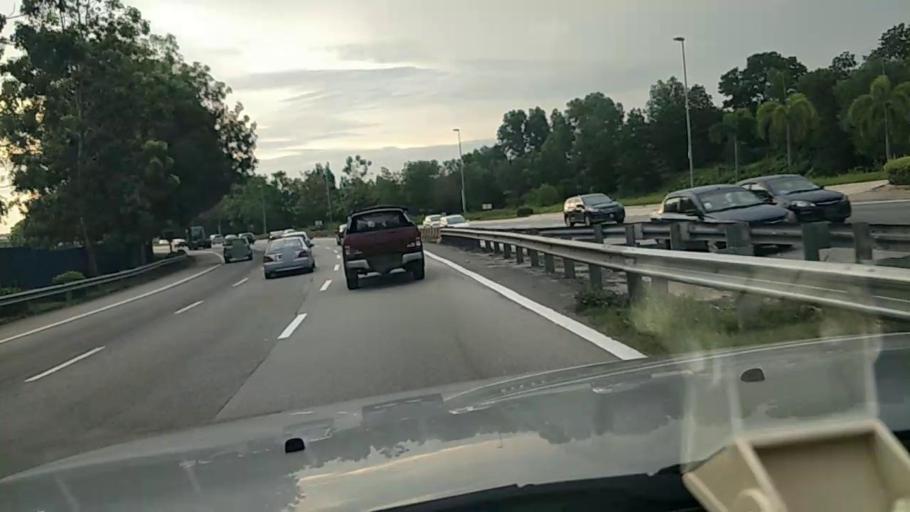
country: MY
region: Selangor
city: Shah Alam
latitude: 3.0990
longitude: 101.4819
